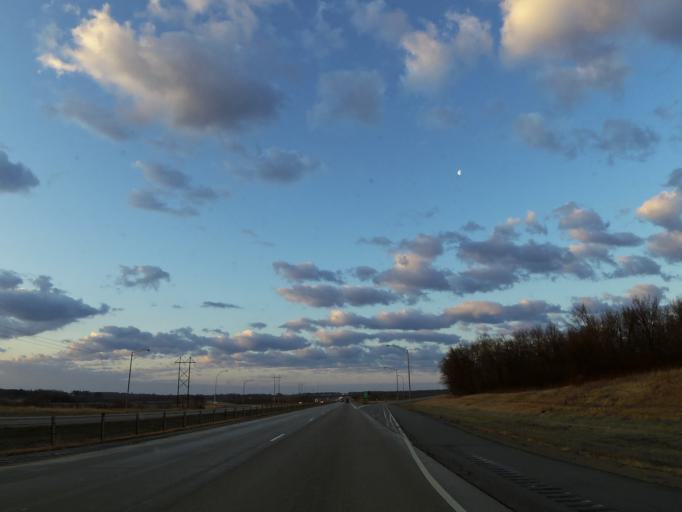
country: US
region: Minnesota
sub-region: Rice County
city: Dundas
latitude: 44.4339
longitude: -93.2927
